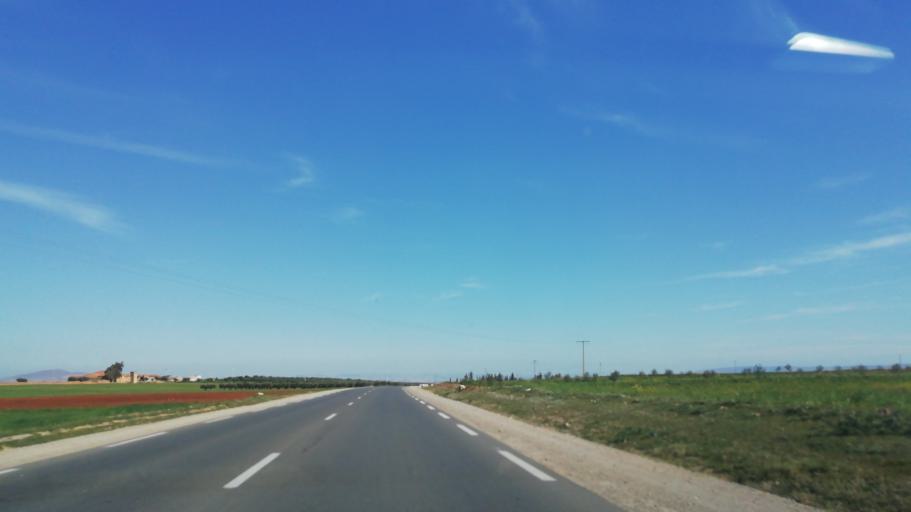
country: DZ
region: Mascara
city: Mascara
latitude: 35.4164
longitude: 0.4007
